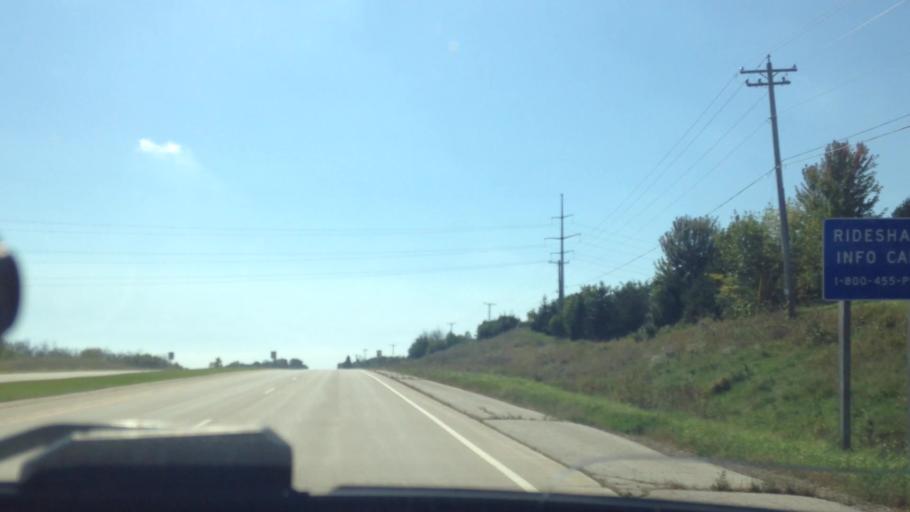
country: US
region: Wisconsin
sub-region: Ozaukee County
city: Port Washington
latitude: 43.3658
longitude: -87.9034
